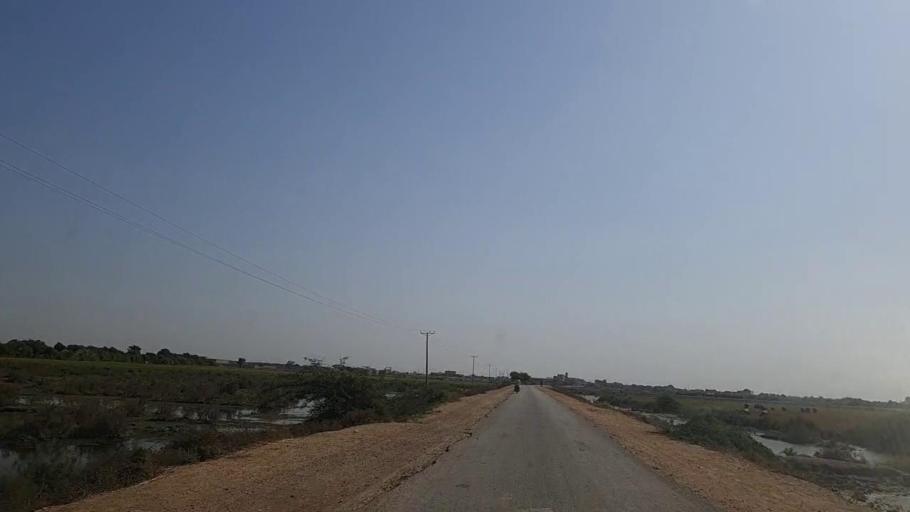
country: PK
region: Sindh
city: Mirpur Batoro
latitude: 24.6257
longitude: 68.2943
